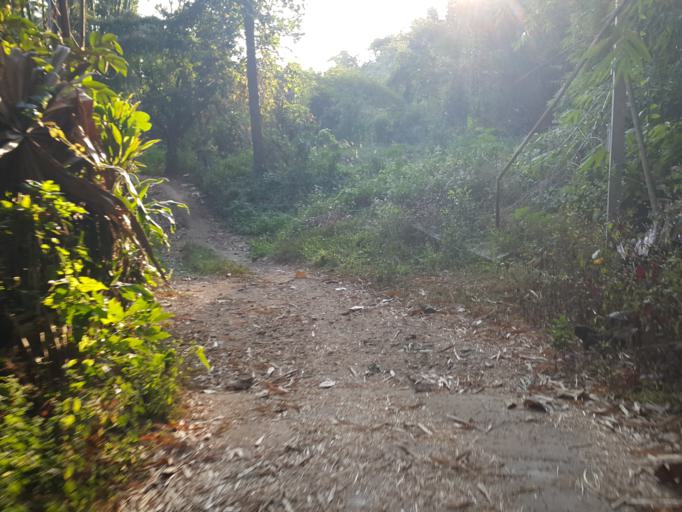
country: TH
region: Chiang Mai
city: Mae On
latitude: 18.7475
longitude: 99.2444
